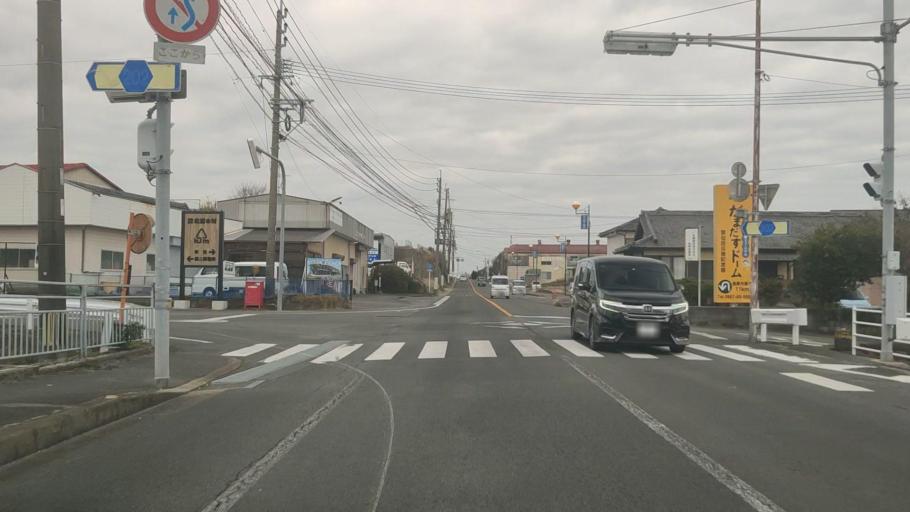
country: JP
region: Nagasaki
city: Shimabara
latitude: 32.8289
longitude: 130.3496
